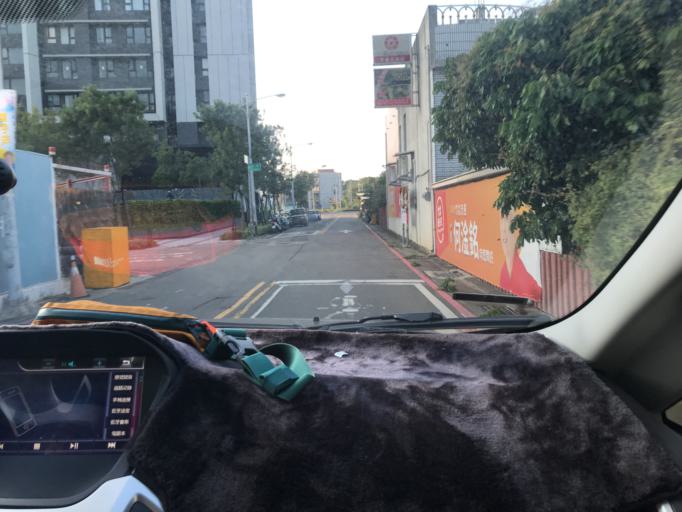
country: TW
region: Taiwan
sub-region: Hsinchu
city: Zhubei
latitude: 24.8258
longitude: 121.0348
